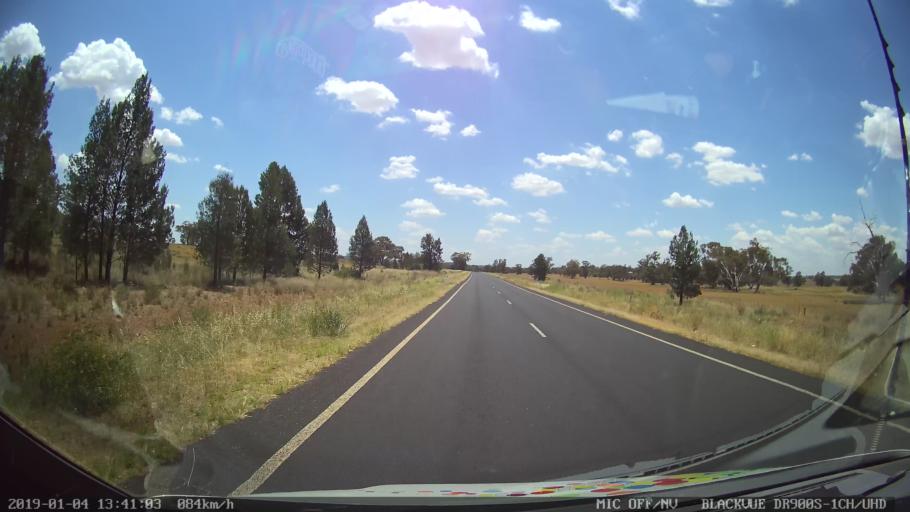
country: AU
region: New South Wales
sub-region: Dubbo Municipality
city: Dubbo
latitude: -32.5071
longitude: 148.5539
